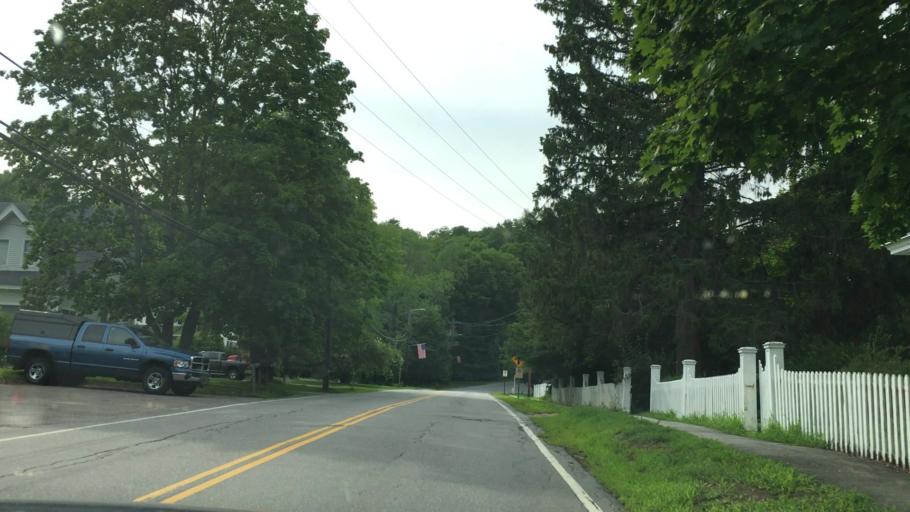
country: US
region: New Hampshire
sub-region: Carroll County
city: Center Harbor
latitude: 43.7096
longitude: -71.4646
